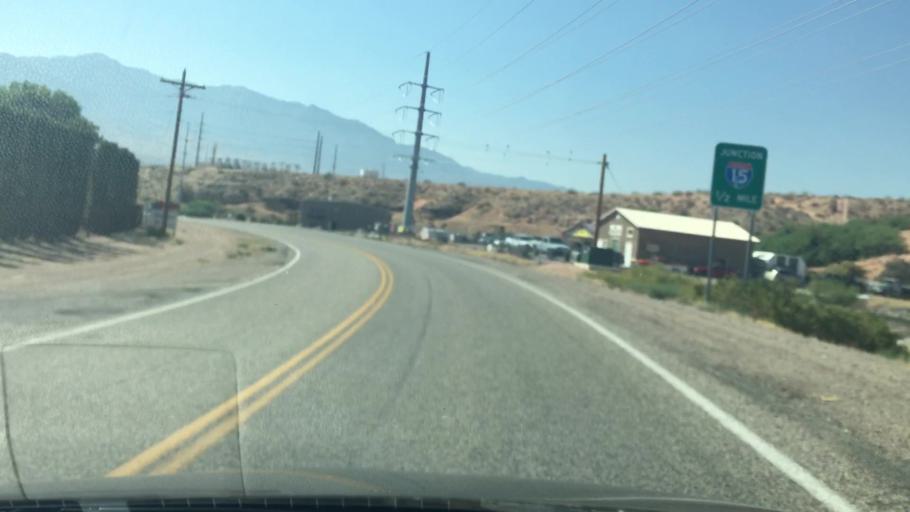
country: US
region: Arizona
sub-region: Mohave County
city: Beaver Dam
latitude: 36.8986
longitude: -113.9347
